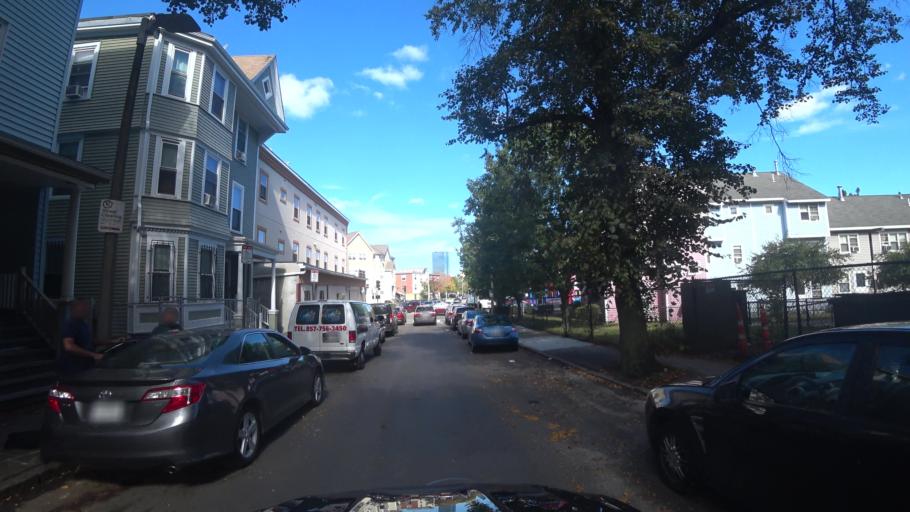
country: US
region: Massachusetts
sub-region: Suffolk County
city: South Boston
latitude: 42.3280
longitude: -71.0793
